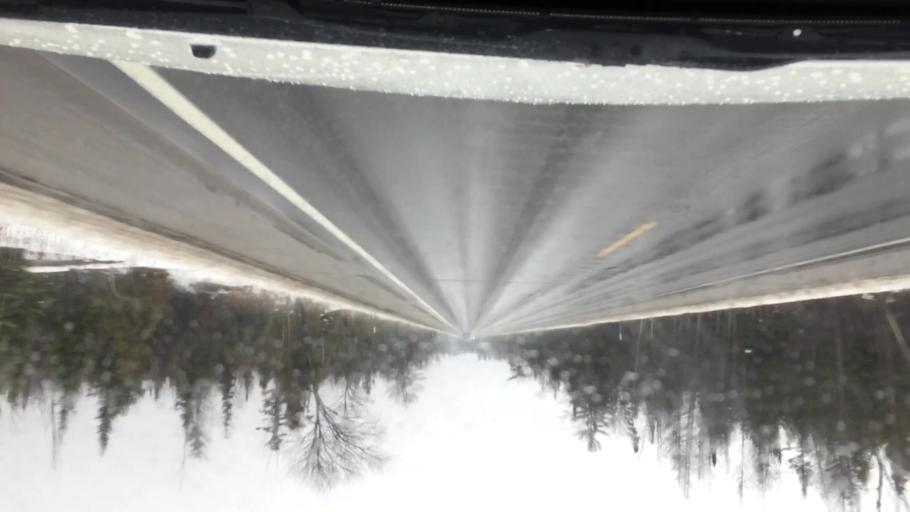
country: US
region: Michigan
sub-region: Kalkaska County
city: Kalkaska
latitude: 44.7086
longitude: -85.1968
